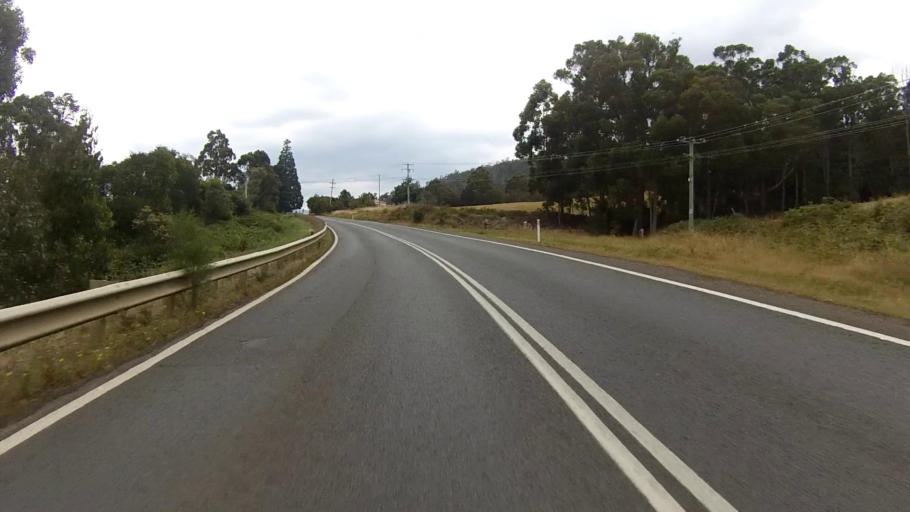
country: AU
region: Tasmania
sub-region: Huon Valley
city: Huonville
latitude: -43.0533
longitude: 147.0490
